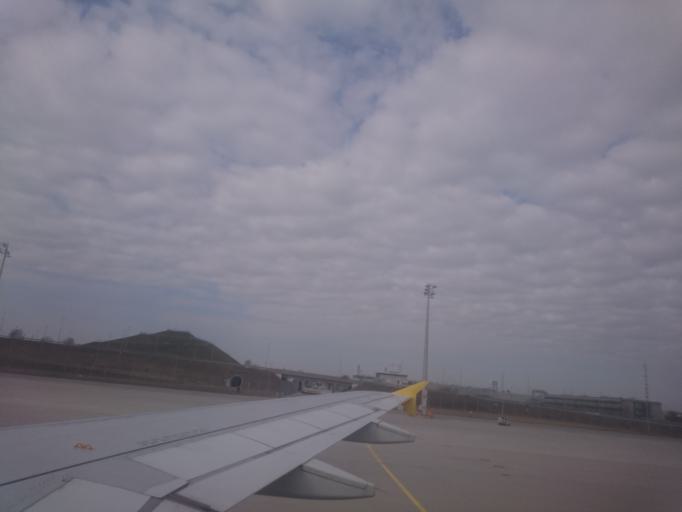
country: DE
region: Bavaria
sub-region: Upper Bavaria
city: Hallbergmoos
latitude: 48.3566
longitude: 11.7772
